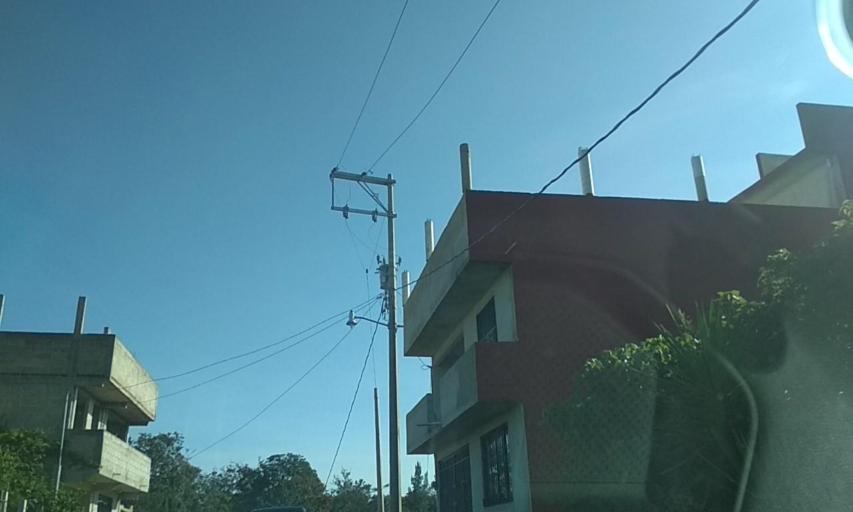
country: MX
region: Veracruz
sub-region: Xalapa
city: Colonia Santa Barbara
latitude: 19.4963
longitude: -96.8742
